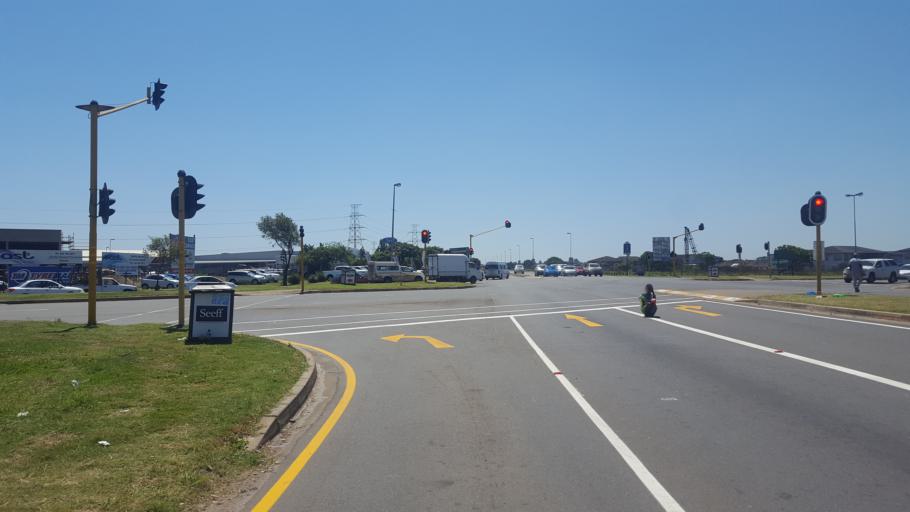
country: ZA
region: KwaZulu-Natal
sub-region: uThungulu District Municipality
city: Richards Bay
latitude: -28.7453
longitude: 32.0513
